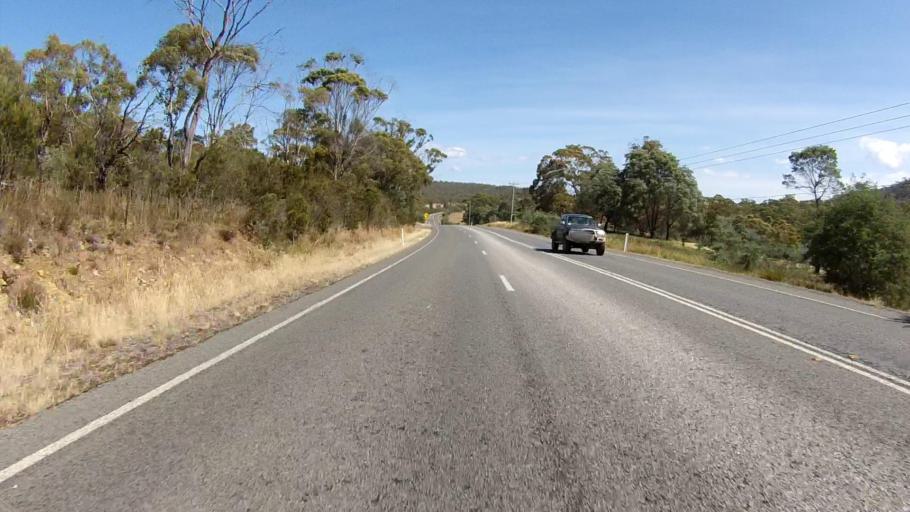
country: AU
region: Tasmania
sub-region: Sorell
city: Sorell
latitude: -42.5731
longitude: 147.8206
